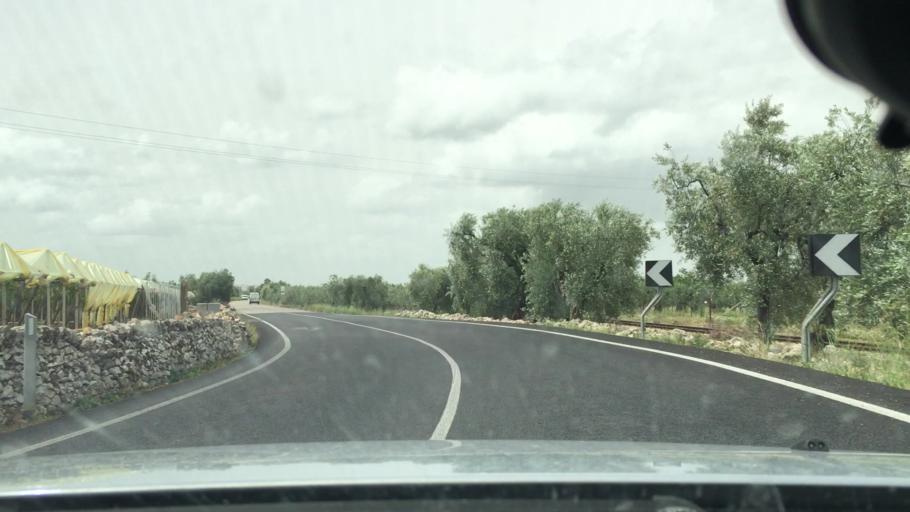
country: IT
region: Apulia
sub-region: Provincia di Bari
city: Capurso
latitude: 41.0418
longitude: 16.9460
